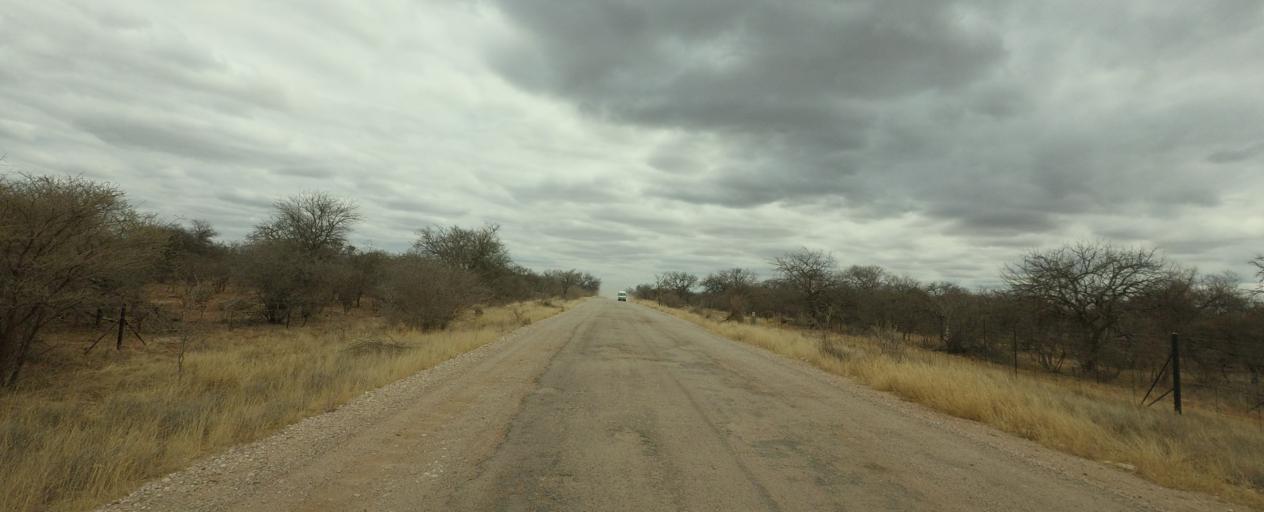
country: BW
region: Central
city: Mogapi
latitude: -22.7800
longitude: 28.3201
